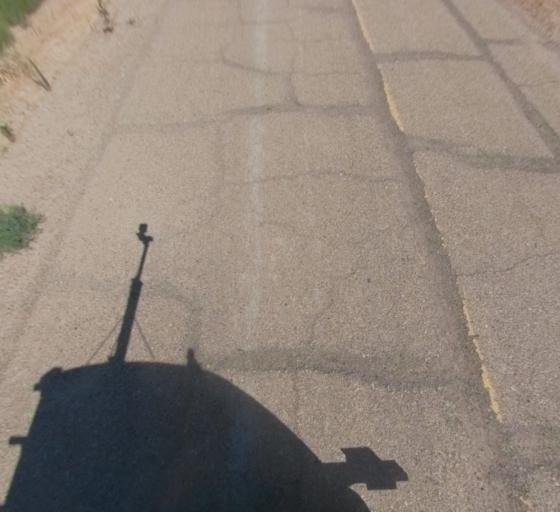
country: US
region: California
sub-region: Fresno County
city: Biola
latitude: 36.8491
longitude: -119.9418
